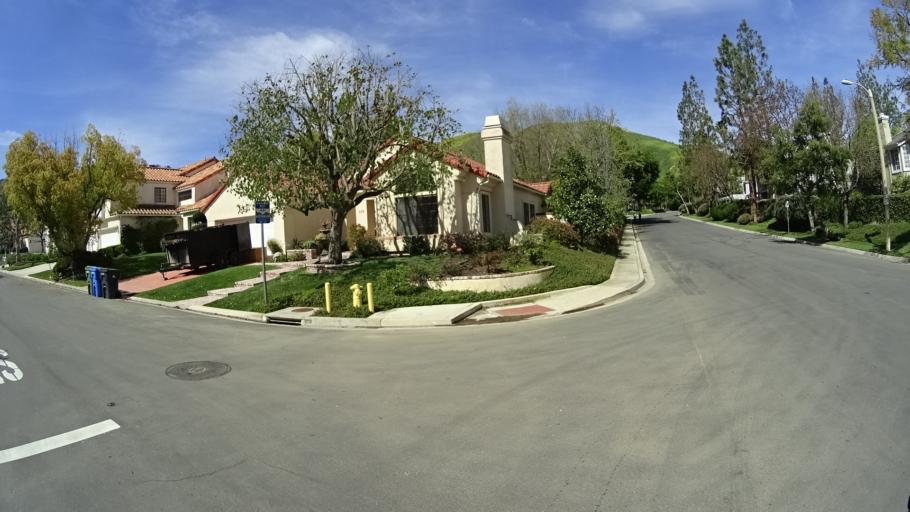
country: US
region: California
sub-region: Ventura County
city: Oak Park
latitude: 34.1758
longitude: -118.7887
